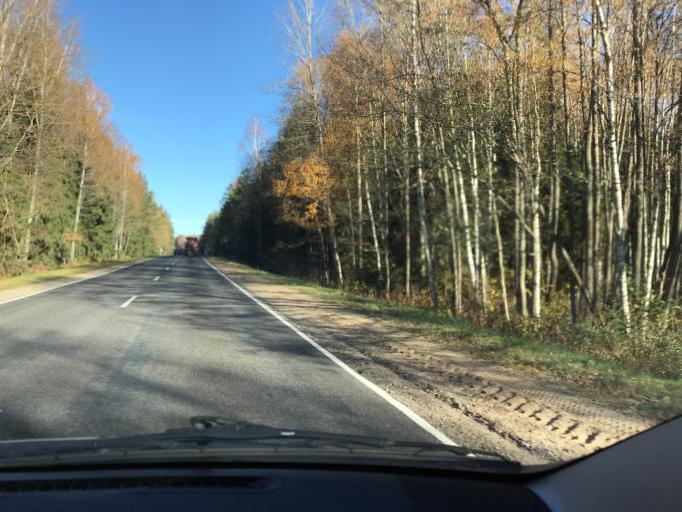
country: BY
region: Vitebsk
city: Polatsk
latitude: 55.3538
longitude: 28.8024
